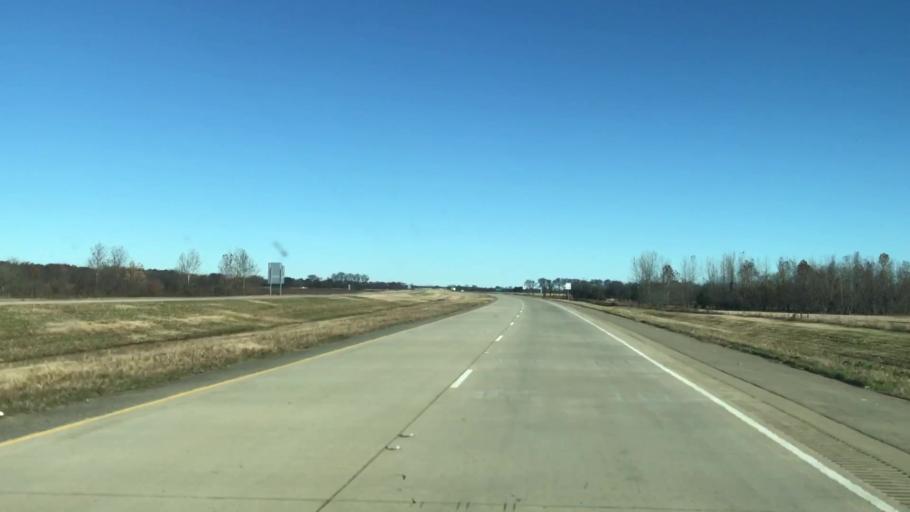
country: US
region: Louisiana
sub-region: Caddo Parish
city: Vivian
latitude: 32.8619
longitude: -93.8604
